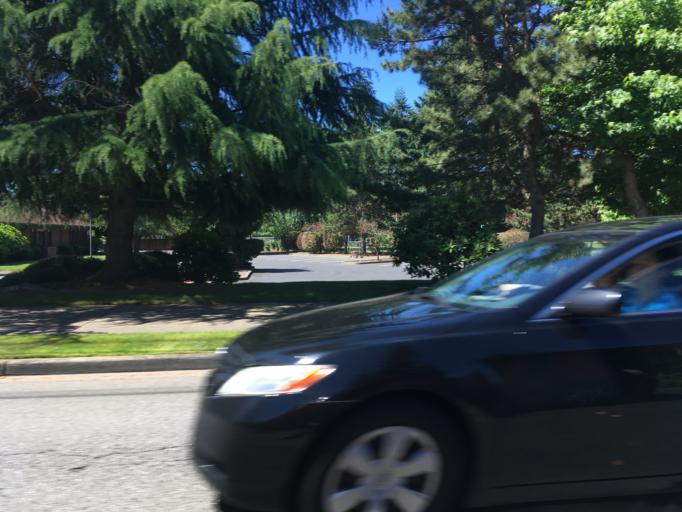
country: US
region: Washington
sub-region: King County
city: Sammamish
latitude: 47.6258
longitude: -122.1257
